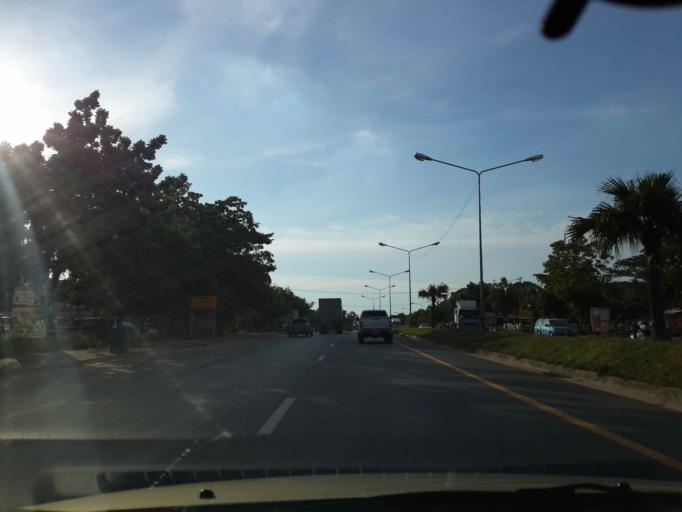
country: TH
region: Chon Buri
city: Bang Lamung
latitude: 12.9992
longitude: 100.9333
